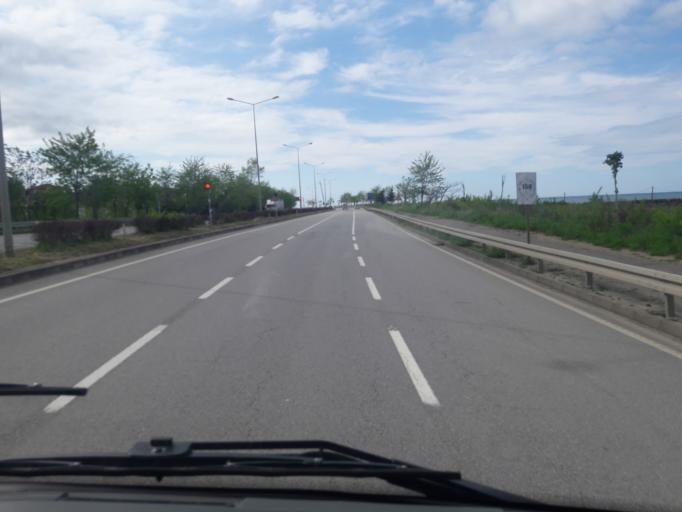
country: TR
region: Giresun
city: Piraziz
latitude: 40.9551
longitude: 38.1205
